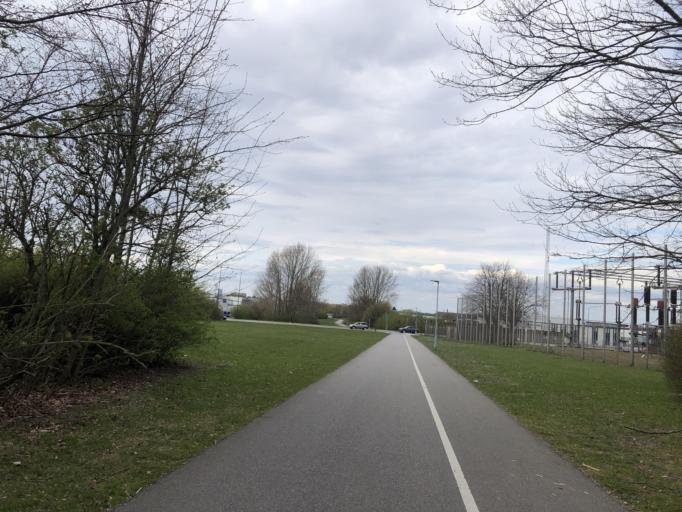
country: SE
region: Skane
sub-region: Malmo
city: Tygelsjo
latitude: 55.5608
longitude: 13.0405
